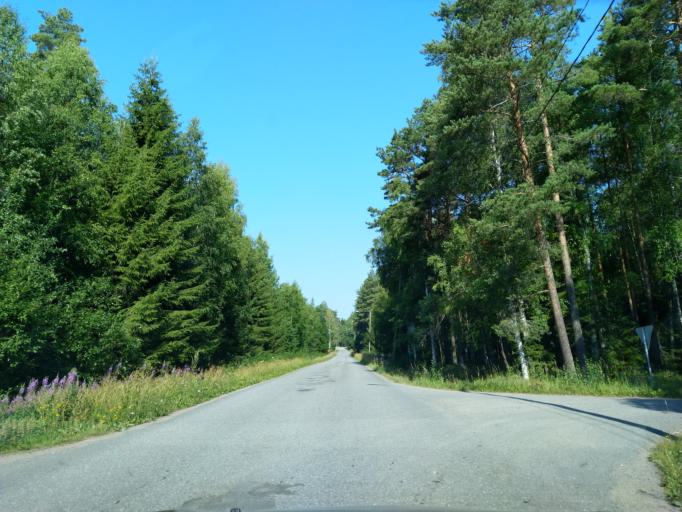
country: FI
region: Satakunta
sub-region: Pori
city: Pomarkku
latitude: 61.6876
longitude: 22.0090
